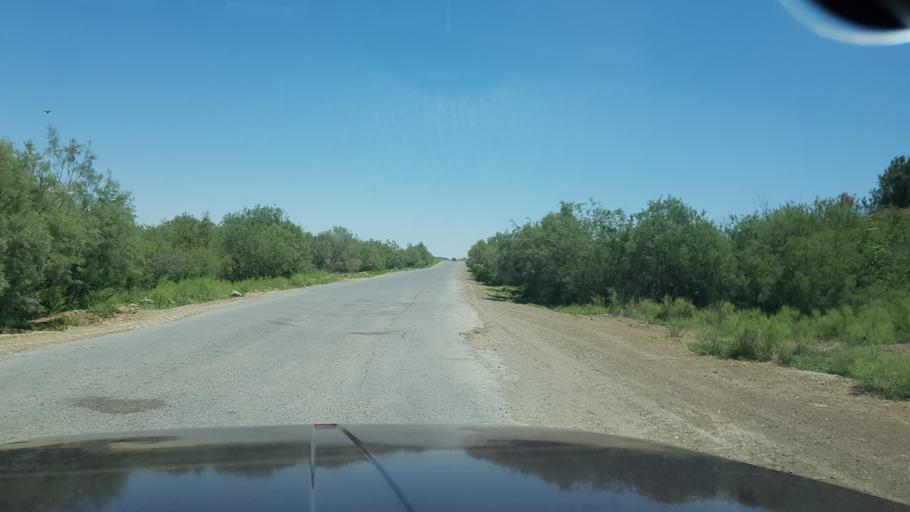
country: TM
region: Ahal
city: Annau
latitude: 37.8849
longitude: 58.7358
